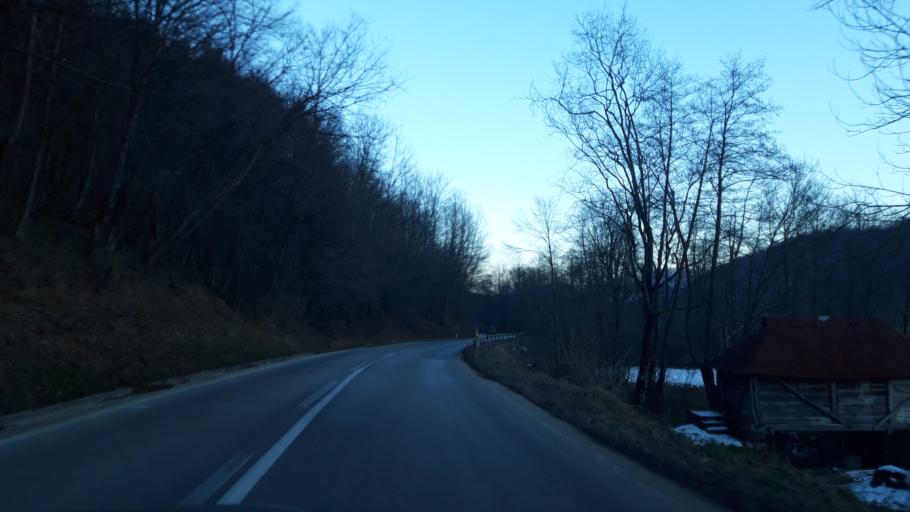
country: BA
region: Republika Srpska
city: Milici
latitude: 44.1695
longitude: 19.0256
